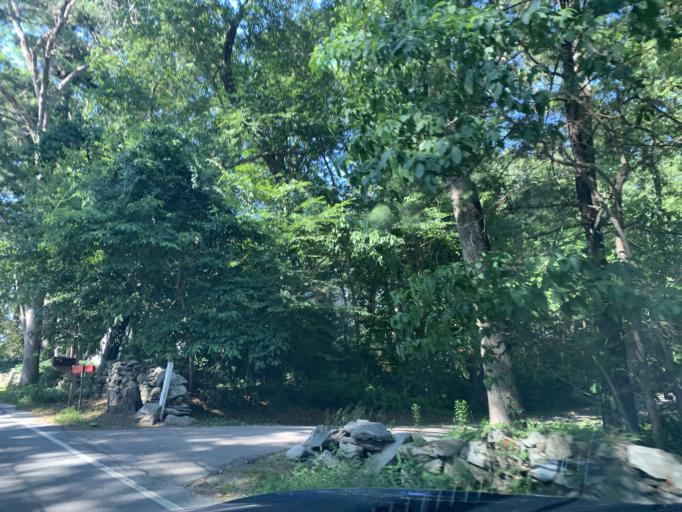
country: US
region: Rhode Island
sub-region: Kent County
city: East Greenwich
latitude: 41.6189
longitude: -71.4435
